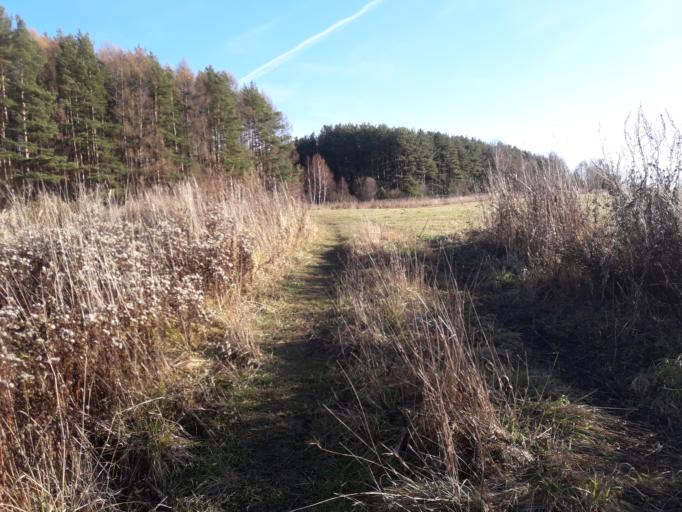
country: RU
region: Moskovskaya
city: Ashukino
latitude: 56.1618
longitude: 37.9672
